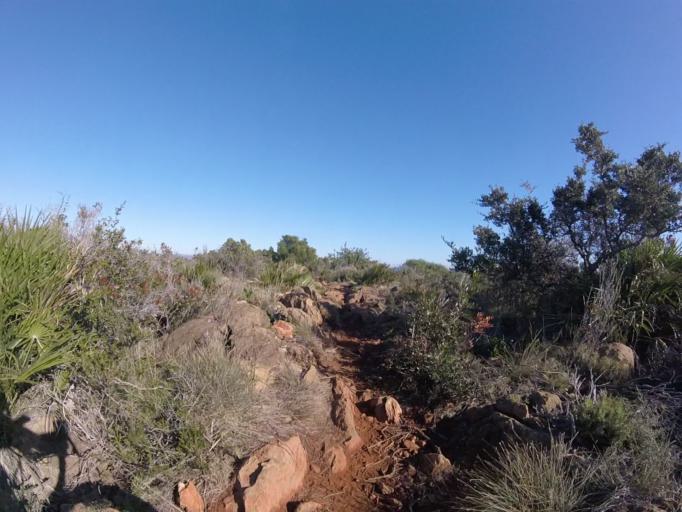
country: ES
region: Valencia
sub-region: Provincia de Castello
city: Orpesa/Oropesa del Mar
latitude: 40.1184
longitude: 0.1192
